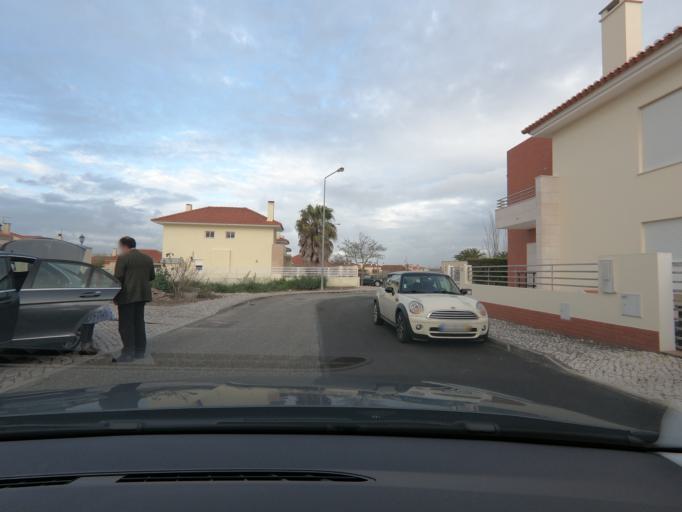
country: PT
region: Lisbon
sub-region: Cascais
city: Sao Domingos de Rana
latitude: 38.7304
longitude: -9.3273
